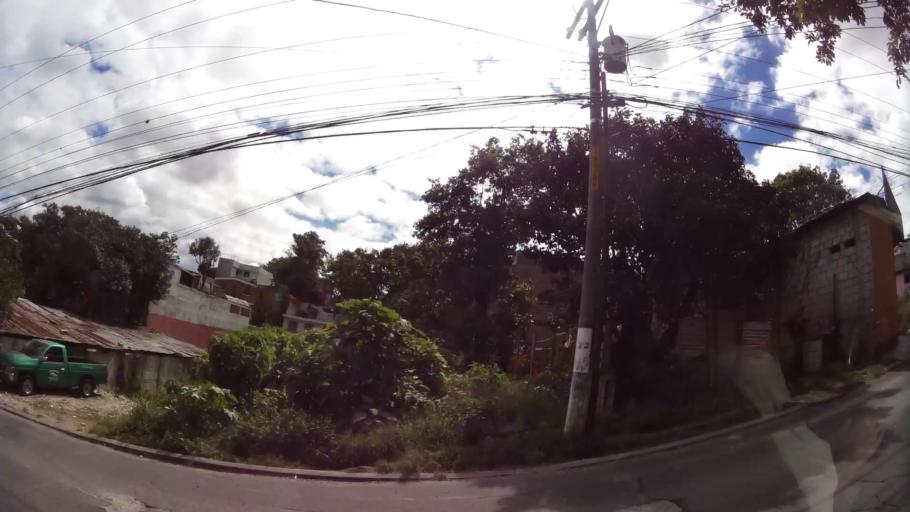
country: GT
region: Guatemala
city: Guatemala City
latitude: 14.6818
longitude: -90.5501
